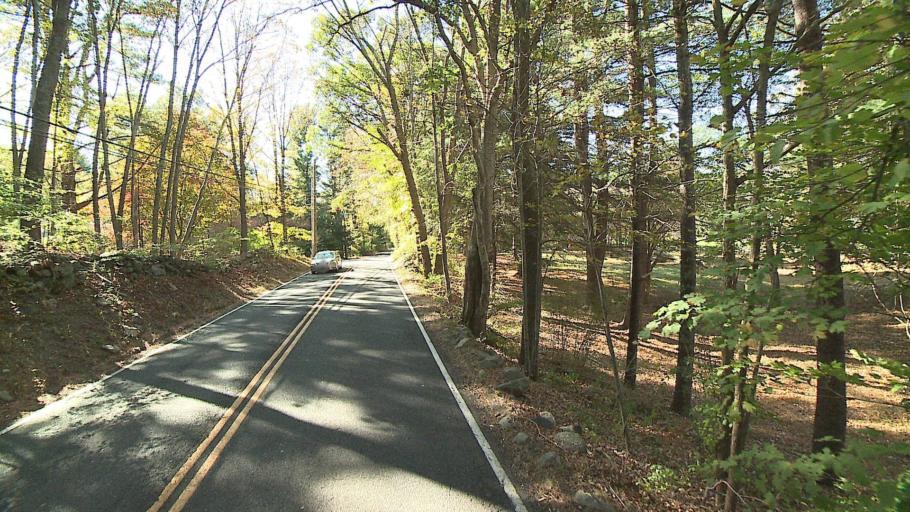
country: US
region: Connecticut
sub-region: Fairfield County
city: Westport
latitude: 41.2243
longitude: -73.3214
